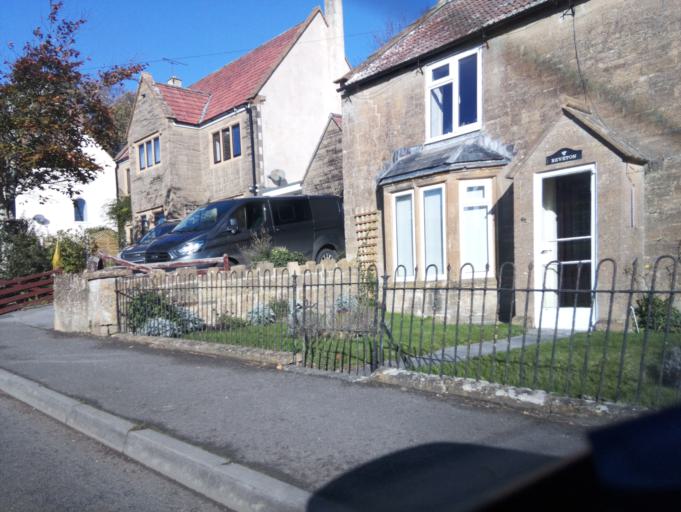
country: GB
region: England
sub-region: Somerset
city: Martock
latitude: 50.9817
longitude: -2.7465
